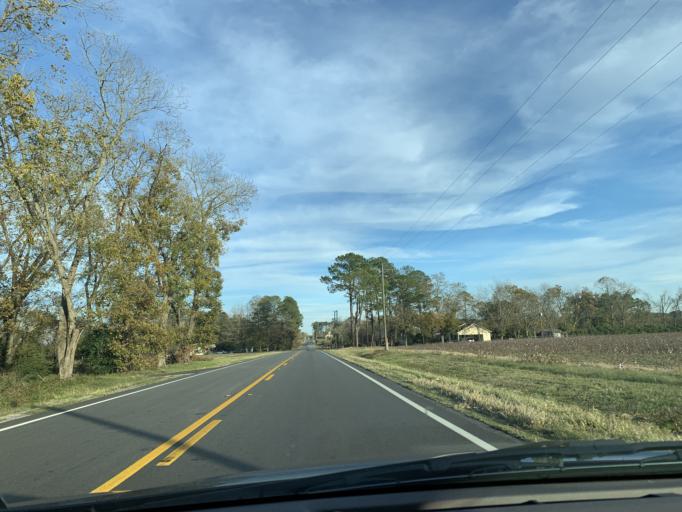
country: US
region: Georgia
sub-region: Irwin County
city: Ocilla
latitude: 31.5926
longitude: -83.2307
